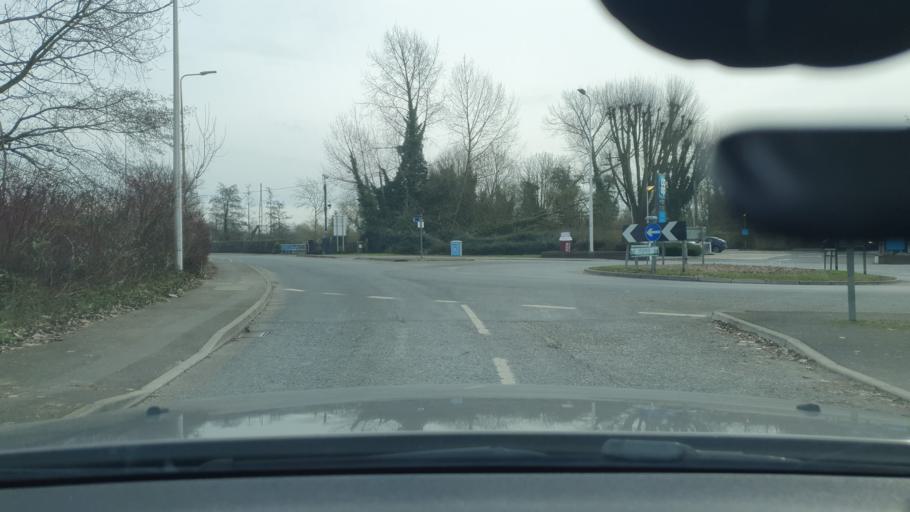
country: GB
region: England
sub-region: West Berkshire
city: Hungerford
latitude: 51.4192
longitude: -1.5108
